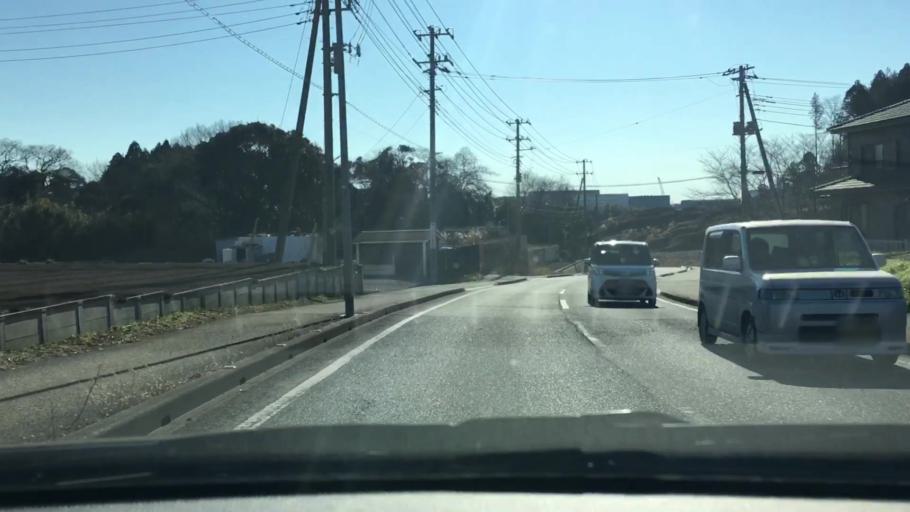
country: JP
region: Chiba
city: Shisui
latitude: 35.7210
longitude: 140.3253
